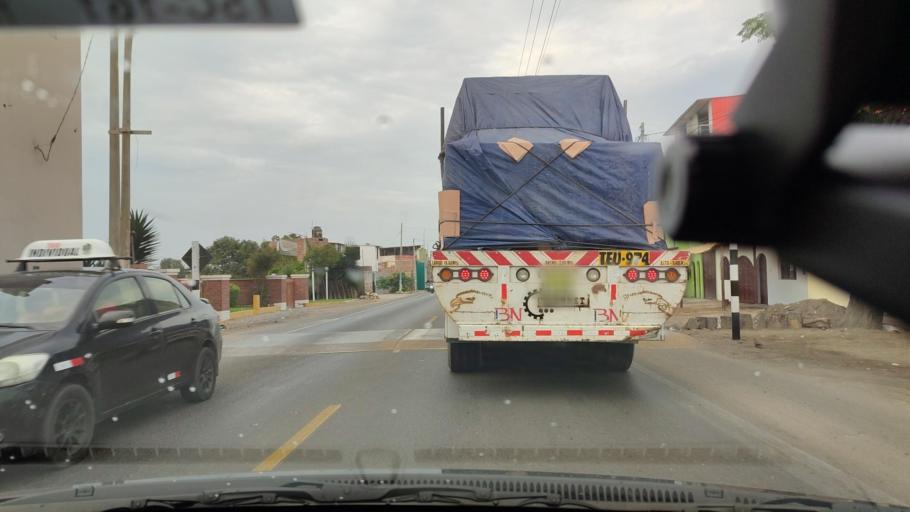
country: PE
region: La Libertad
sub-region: Provincia de Trujillo
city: Buenos Aires
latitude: -8.1344
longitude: -79.0251
